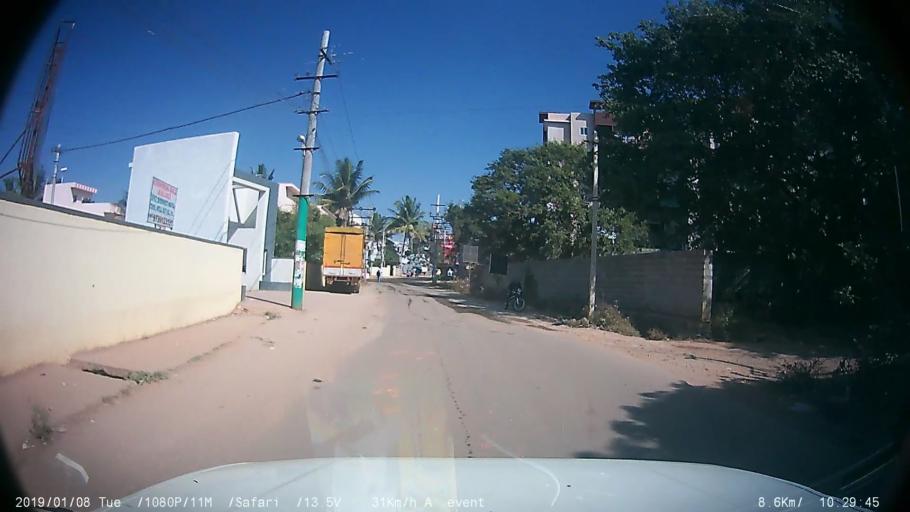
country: IN
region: Karnataka
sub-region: Bangalore Urban
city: Anekal
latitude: 12.8313
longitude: 77.6552
